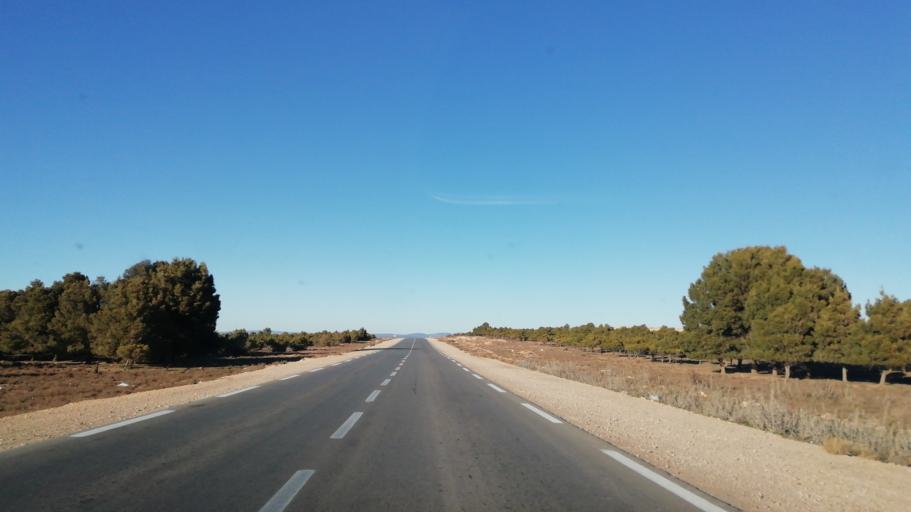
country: DZ
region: Tlemcen
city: Sebdou
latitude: 34.4418
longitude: -1.2761
